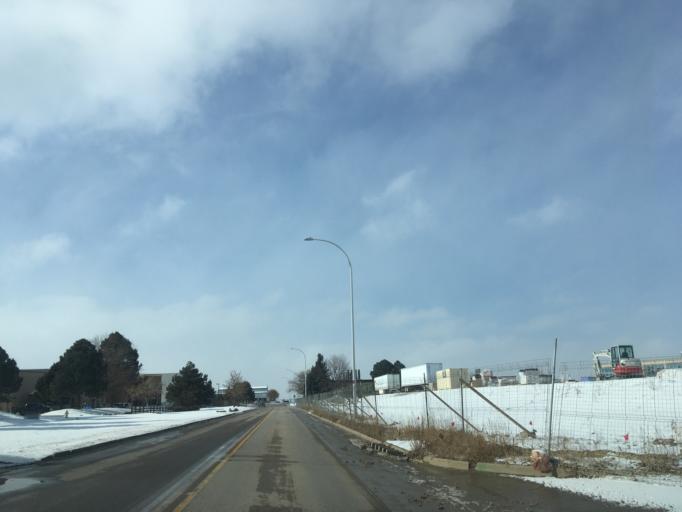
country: US
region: Colorado
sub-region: Broomfield County
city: Broomfield
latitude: 39.9110
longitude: -105.1049
